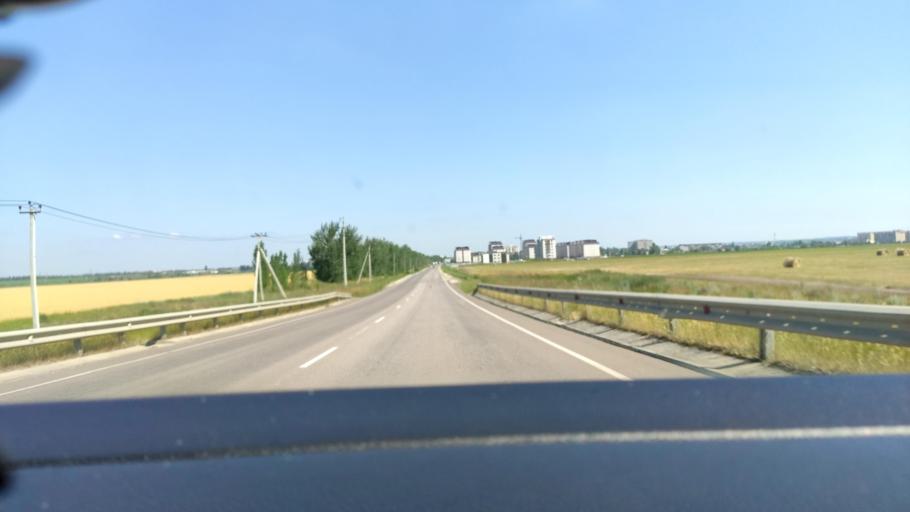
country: RU
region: Voronezj
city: Novaya Usman'
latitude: 51.5942
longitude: 39.3738
